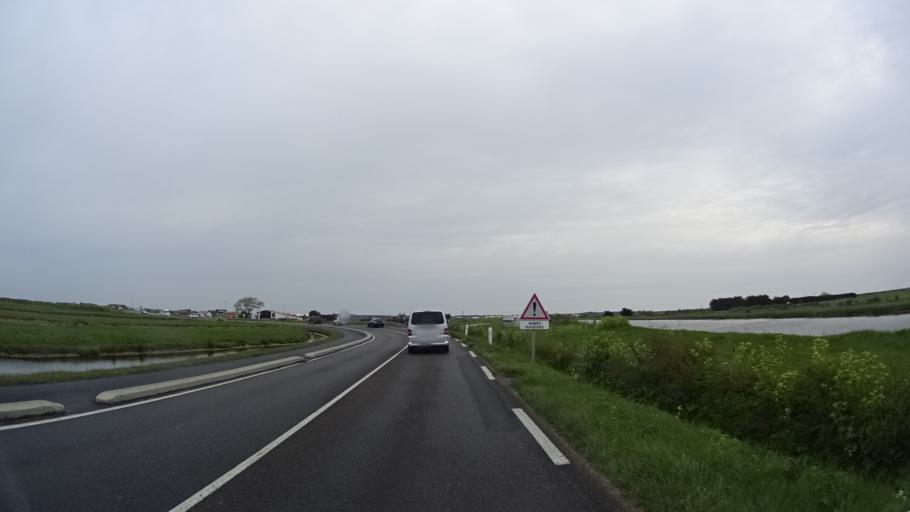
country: FR
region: Pays de la Loire
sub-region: Departement de la Vendee
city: La Gueriniere
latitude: 46.9819
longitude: -2.2463
